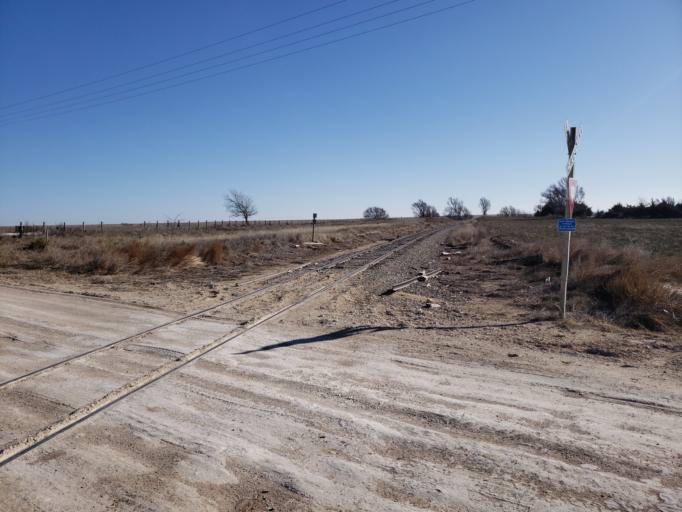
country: US
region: Kansas
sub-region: Lane County
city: Dighton
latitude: 38.4445
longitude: -100.1914
